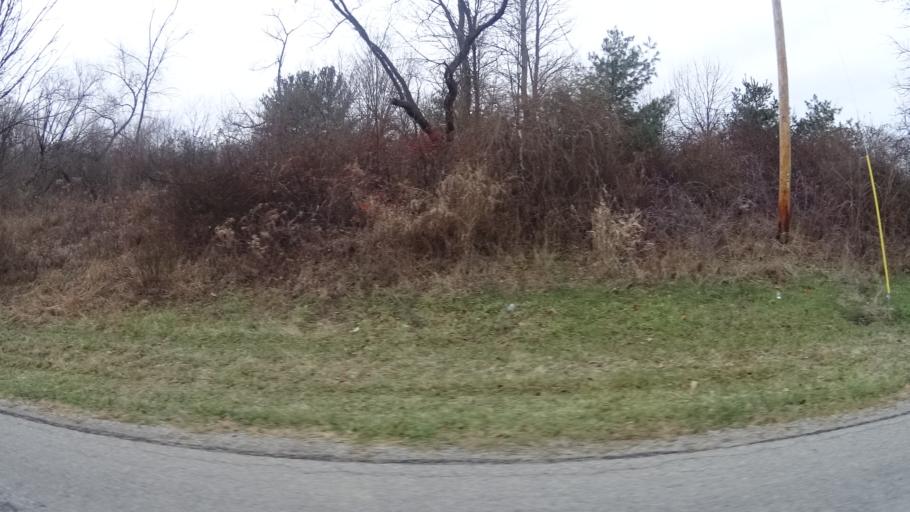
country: US
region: Ohio
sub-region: Lorain County
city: Wellington
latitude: 41.1799
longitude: -82.1932
